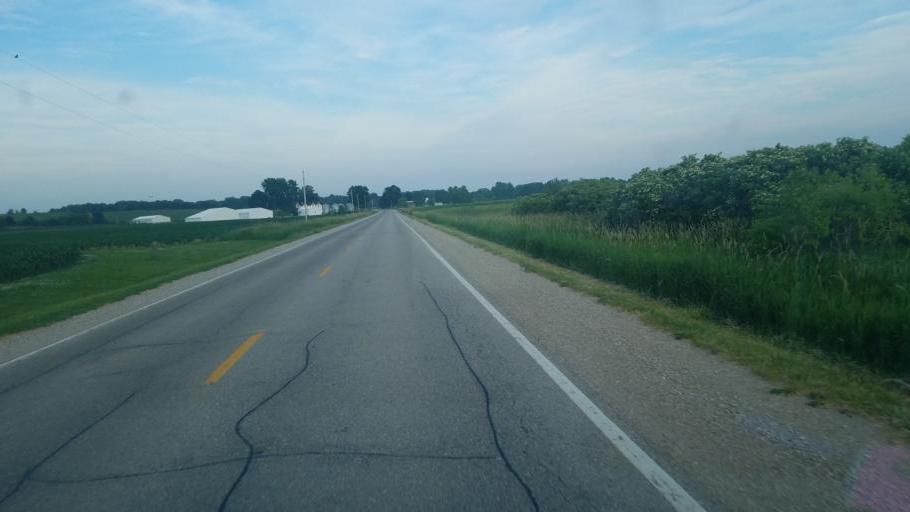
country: US
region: Iowa
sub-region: Benton County
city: Belle Plaine
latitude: 41.9387
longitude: -92.4095
